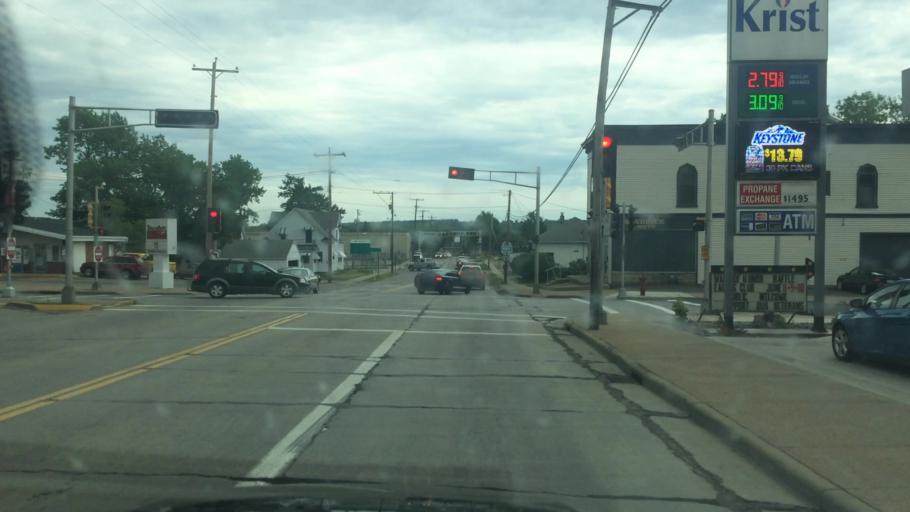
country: US
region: Wisconsin
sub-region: Marathon County
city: Wausau
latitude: 44.9484
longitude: -89.6398
